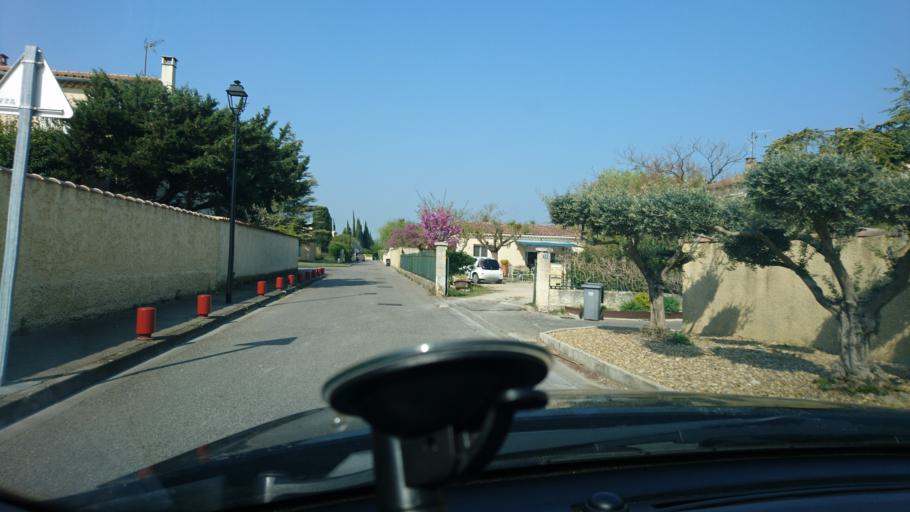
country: FR
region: Provence-Alpes-Cote d'Azur
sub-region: Departement des Bouches-du-Rhone
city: Saint-Andiol
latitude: 43.8329
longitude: 4.9027
